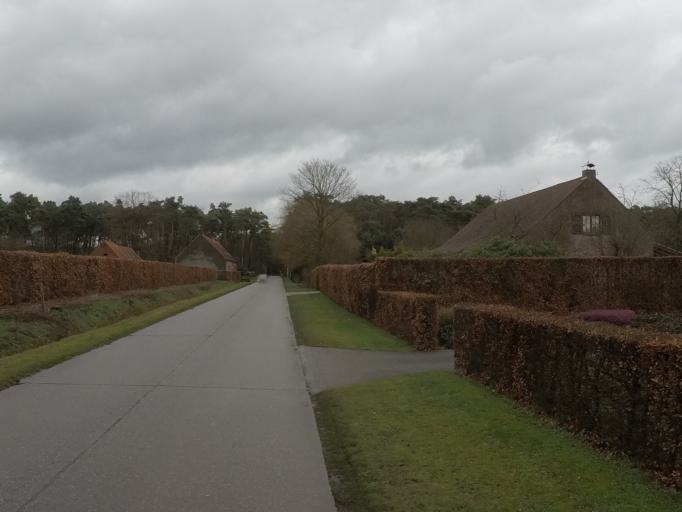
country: BE
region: Flanders
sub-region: Provincie Antwerpen
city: Zandhoven
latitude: 51.2260
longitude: 4.6349
